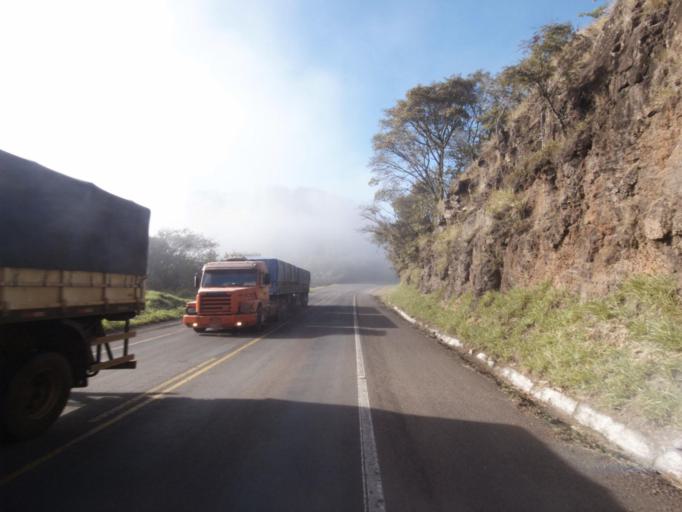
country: BR
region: Rio Grande do Sul
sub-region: Frederico Westphalen
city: Frederico Westphalen
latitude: -26.8153
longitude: -53.4316
